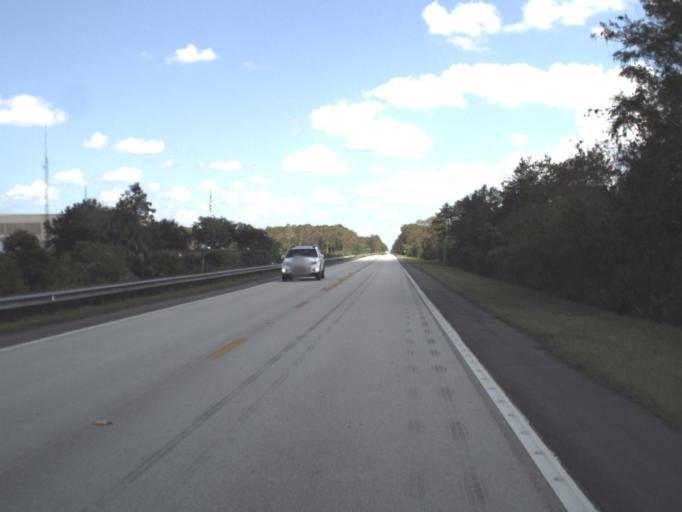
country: US
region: Florida
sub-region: Miami-Dade County
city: Kendall West
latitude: 25.8571
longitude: -81.0355
